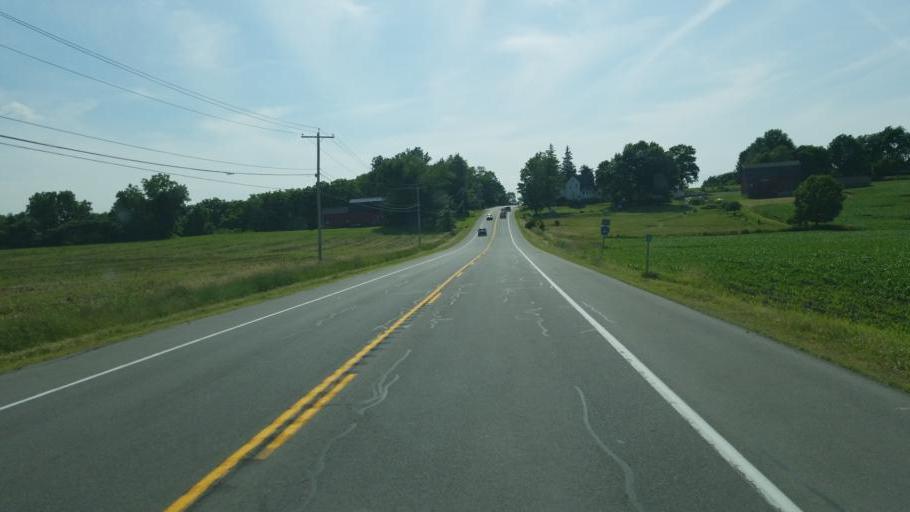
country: US
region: New York
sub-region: Livingston County
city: Lima
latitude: 42.9096
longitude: -77.5670
